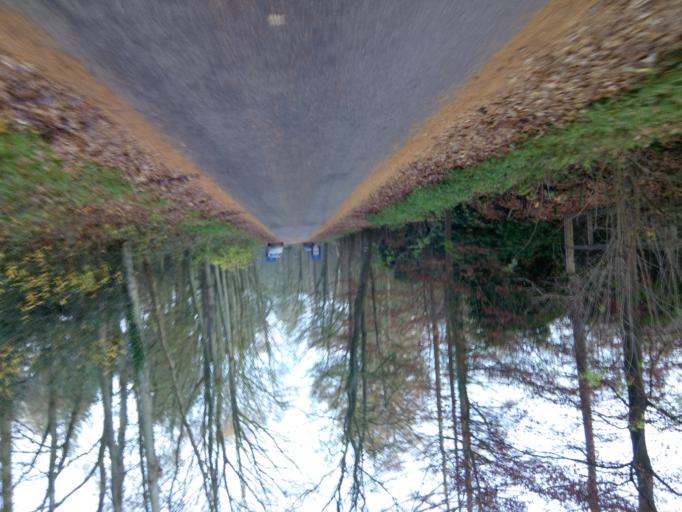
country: NL
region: Utrecht
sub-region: Gemeente Amersfoort
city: Randenbroek
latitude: 52.1209
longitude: 5.3963
